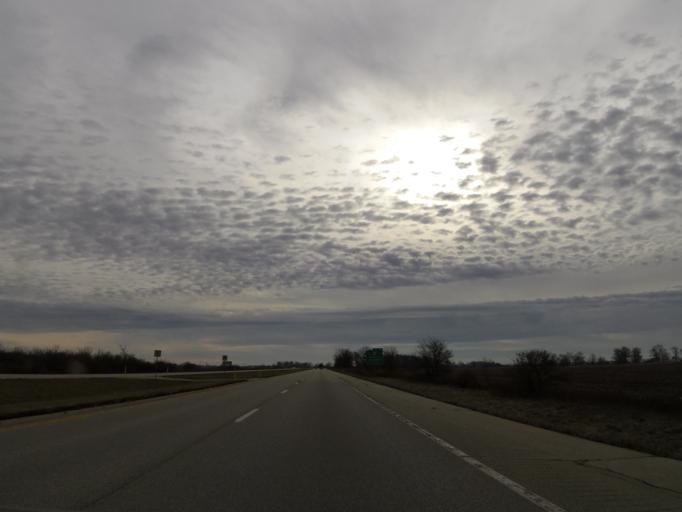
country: US
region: Indiana
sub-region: Boone County
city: Thorntown
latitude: 39.9515
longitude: -86.6359
